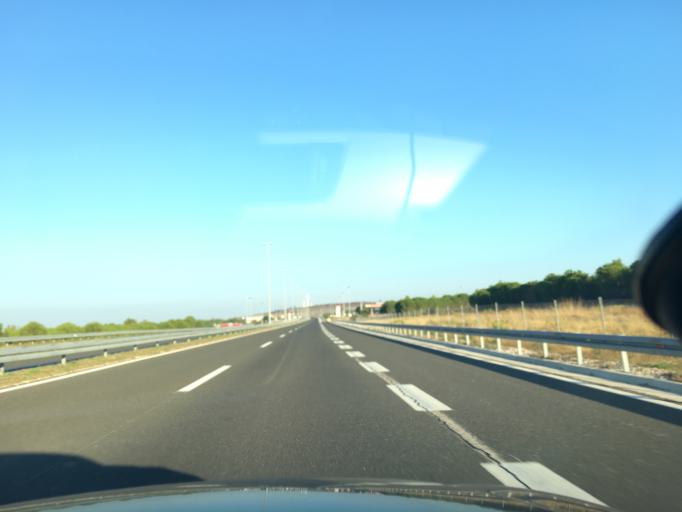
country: HR
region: Sibensko-Kniniska
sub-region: Grad Sibenik
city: Brodarica
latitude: 43.6881
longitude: 16.0437
